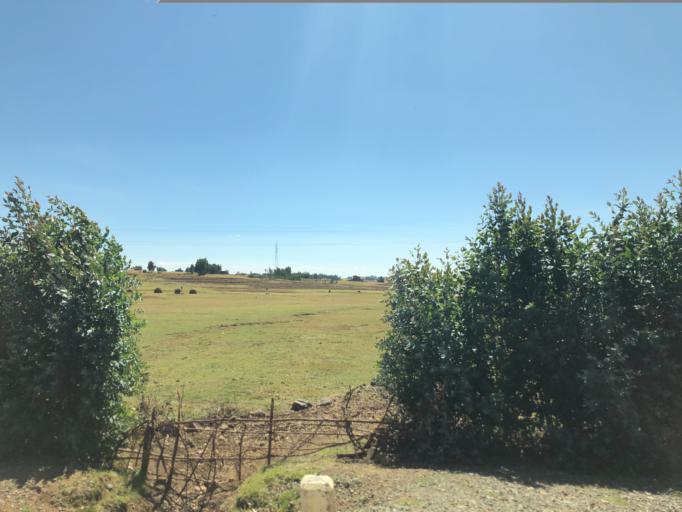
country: ET
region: Amhara
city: Lalibela
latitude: 11.6786
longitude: 38.8985
